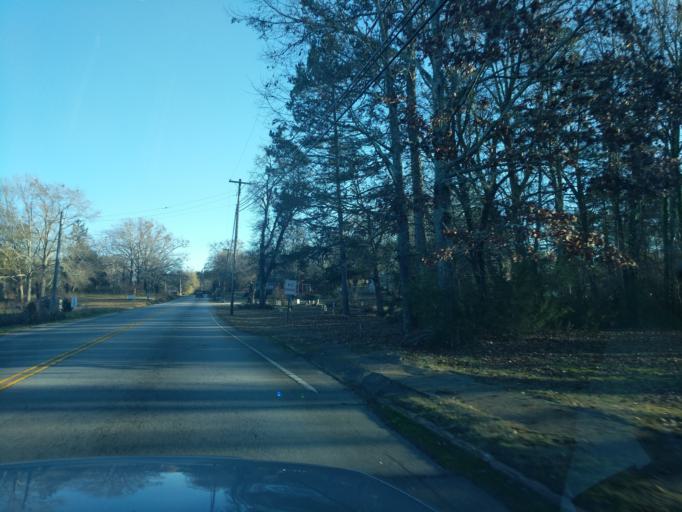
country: US
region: South Carolina
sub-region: Oconee County
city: Westminster
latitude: 34.6544
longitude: -83.0854
